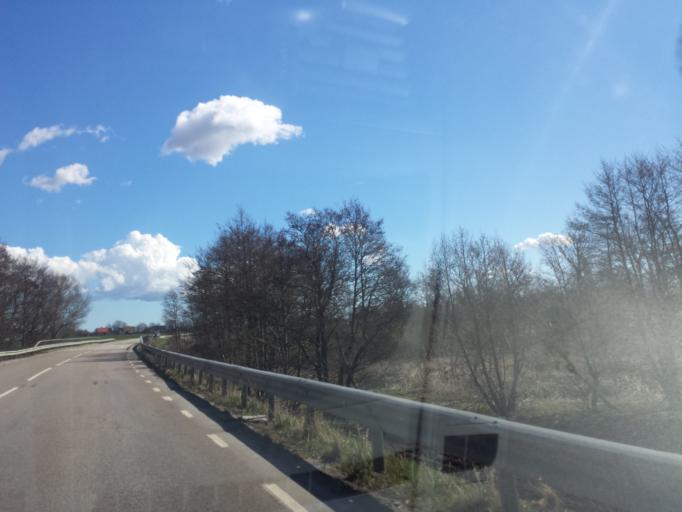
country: SE
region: Skane
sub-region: Ystads Kommun
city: Kopingebro
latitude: 55.4664
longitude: 13.9335
